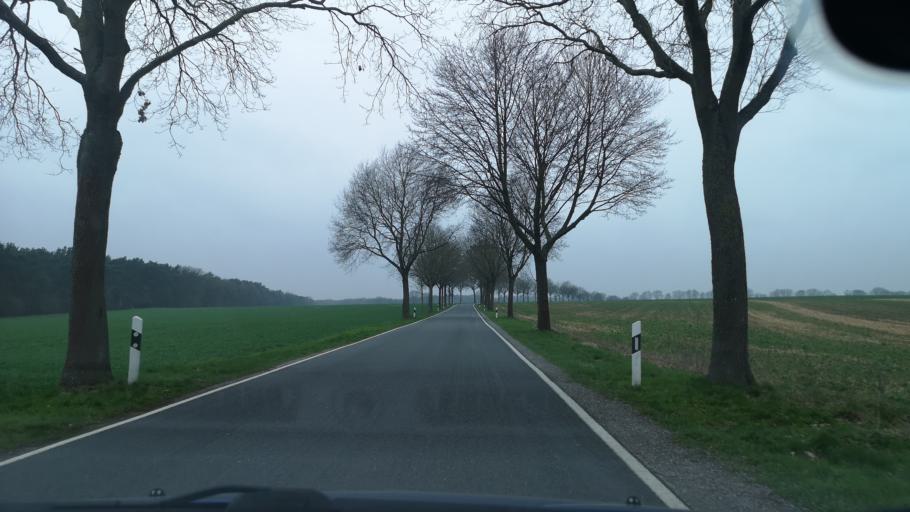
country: DE
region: Lower Saxony
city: Neustadt am Rubenberge
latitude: 52.5640
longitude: 9.4584
